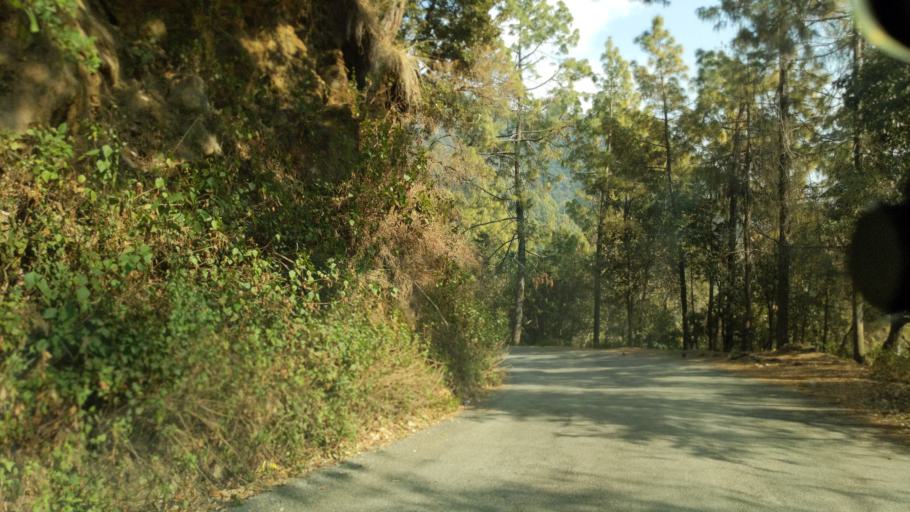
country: IN
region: Uttarakhand
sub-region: Naini Tal
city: Bhowali
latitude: 29.4058
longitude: 79.5380
